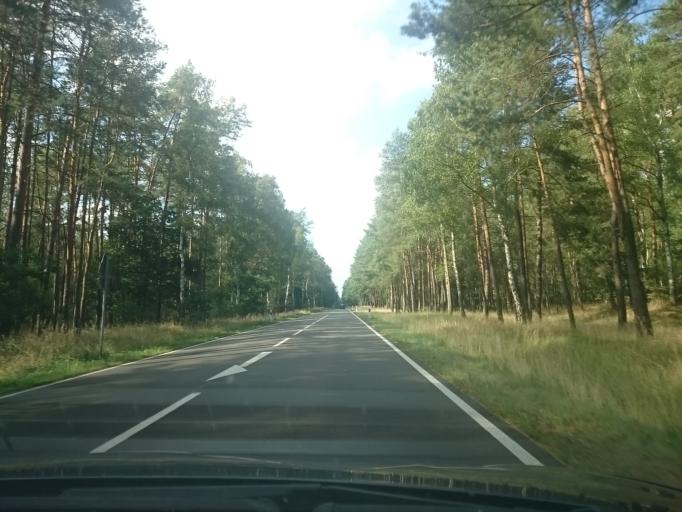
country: DE
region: Mecklenburg-Vorpommern
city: Viereck
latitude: 53.5944
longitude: 14.0592
